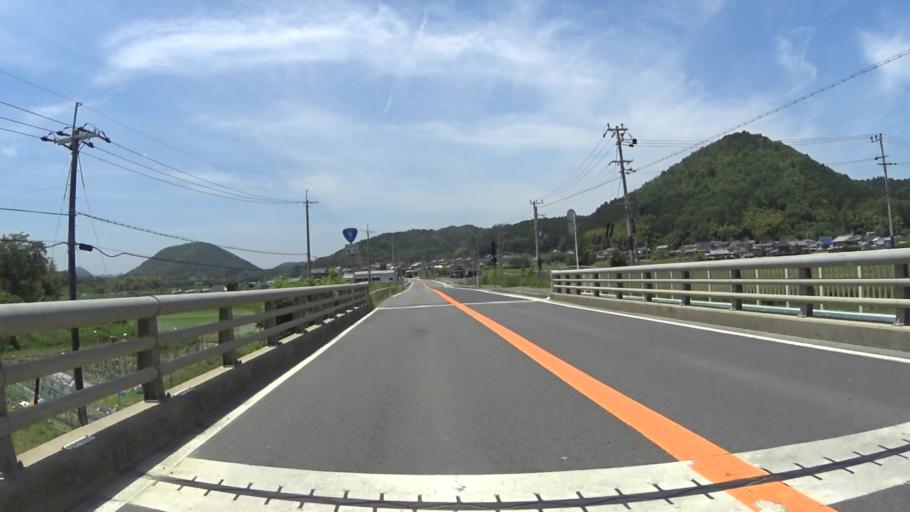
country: JP
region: Kyoto
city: Ayabe
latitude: 35.1746
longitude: 135.4094
